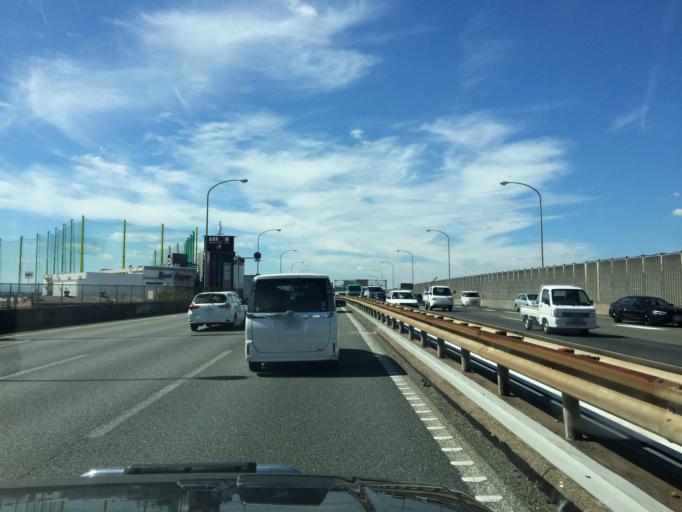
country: JP
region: Osaka
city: Matsubara
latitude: 34.5872
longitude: 135.5732
